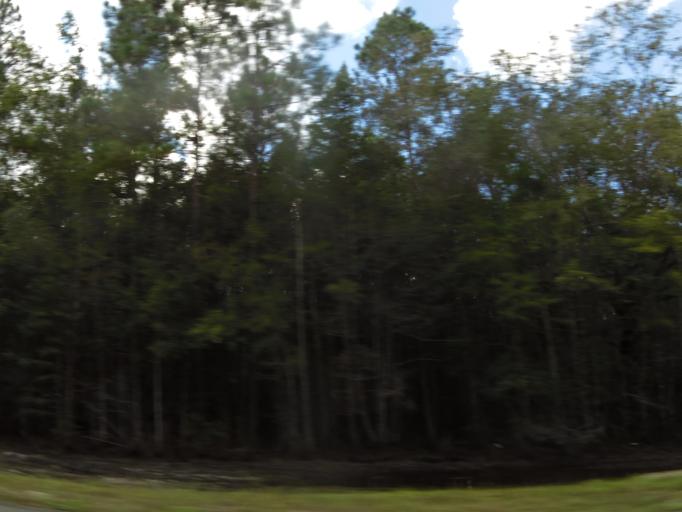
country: US
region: Georgia
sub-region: Charlton County
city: Folkston
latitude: 30.9763
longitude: -82.0250
